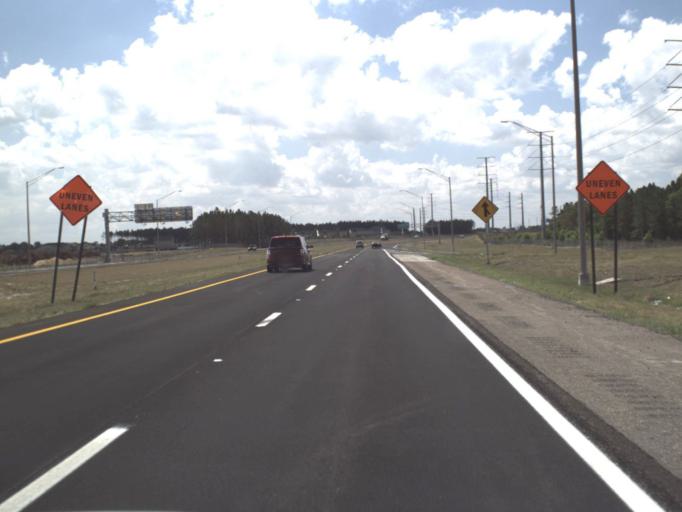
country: US
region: Florida
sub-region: Orange County
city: Oakland
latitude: 28.4705
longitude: -81.6317
